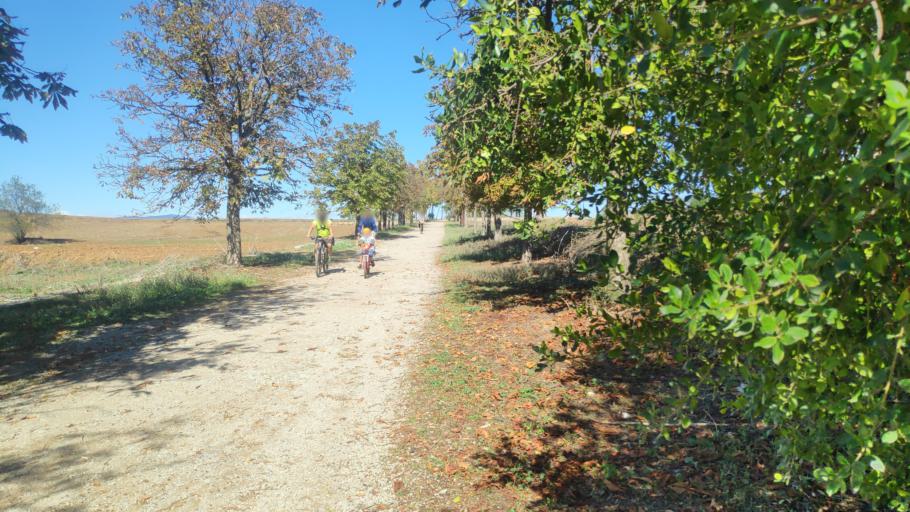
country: ES
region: Catalonia
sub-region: Provincia de Barcelona
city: Mollet del Valles
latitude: 41.5381
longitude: 2.2007
